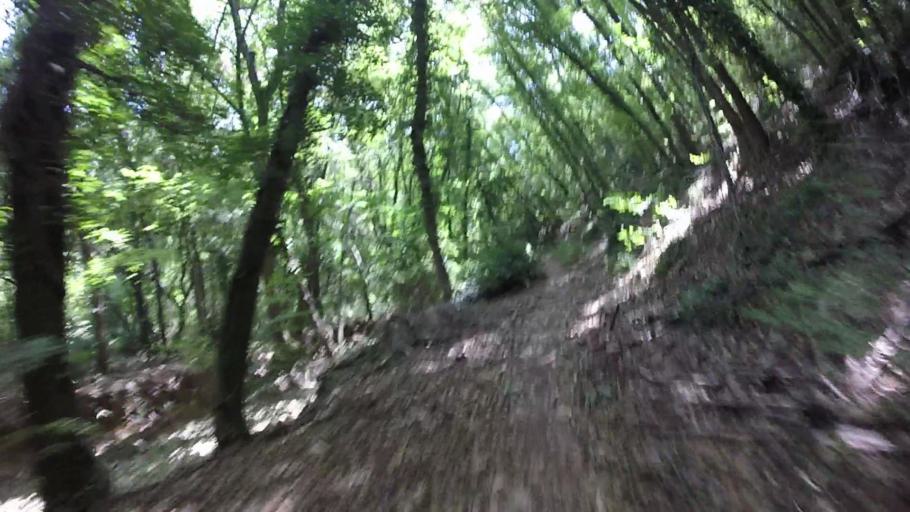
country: FR
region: Provence-Alpes-Cote d'Azur
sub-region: Departement des Alpes-Maritimes
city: Valbonne
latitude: 43.6211
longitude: 7.0262
